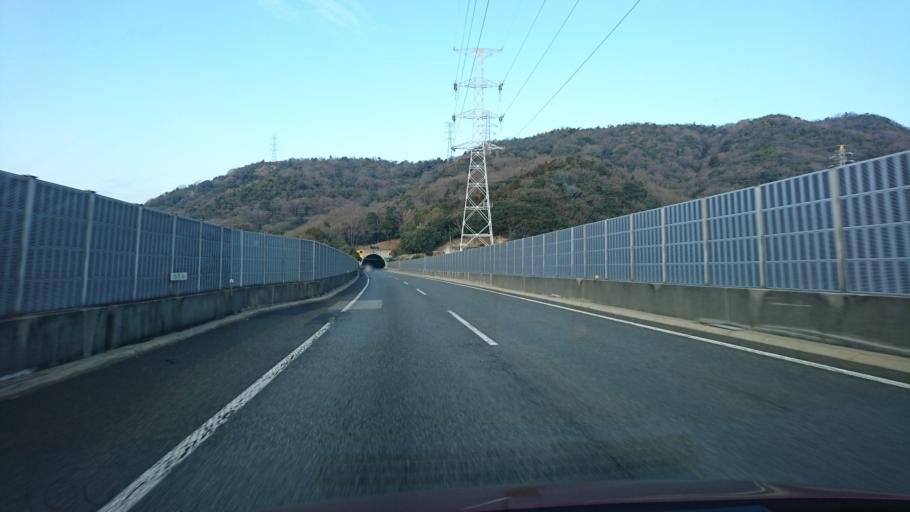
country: JP
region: Hyogo
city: Himeji
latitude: 34.8601
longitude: 134.7213
